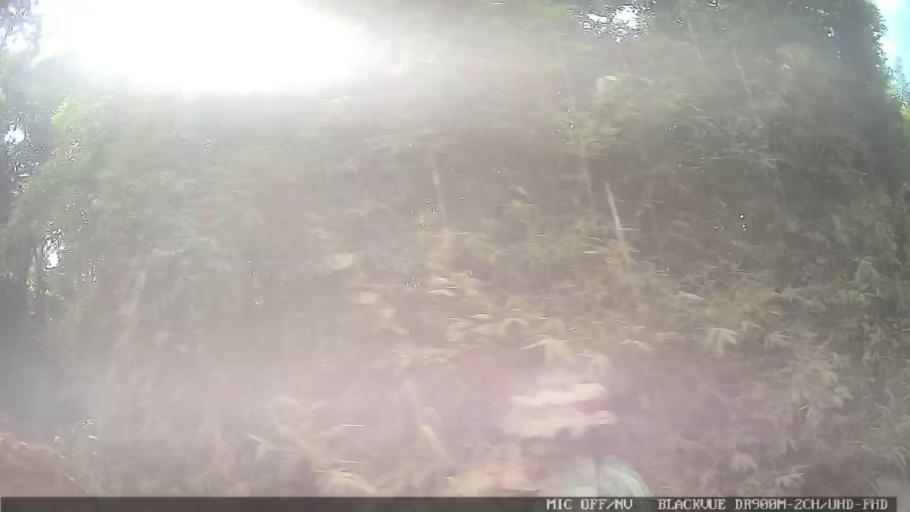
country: BR
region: Sao Paulo
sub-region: Braganca Paulista
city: Braganca Paulista
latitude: -22.9811
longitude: -46.6424
